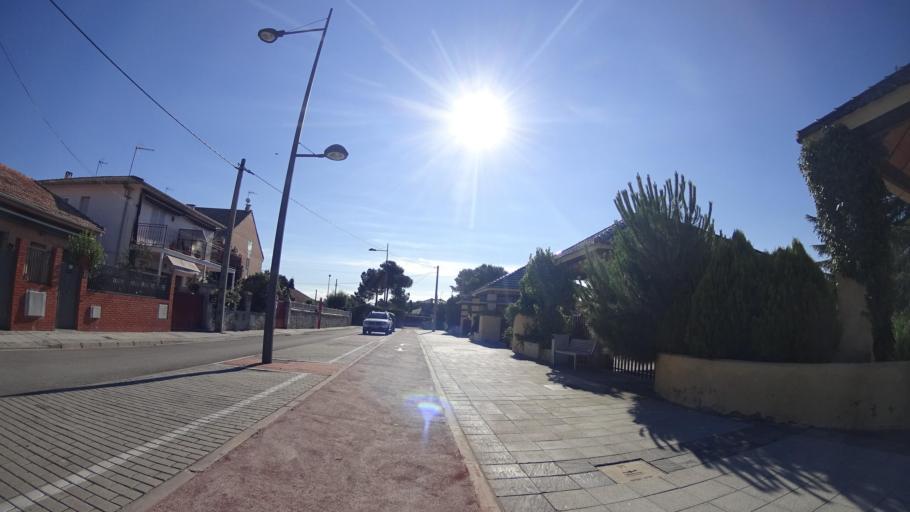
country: ES
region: Madrid
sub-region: Provincia de Madrid
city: Las Matas
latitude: 40.5532
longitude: -3.8930
